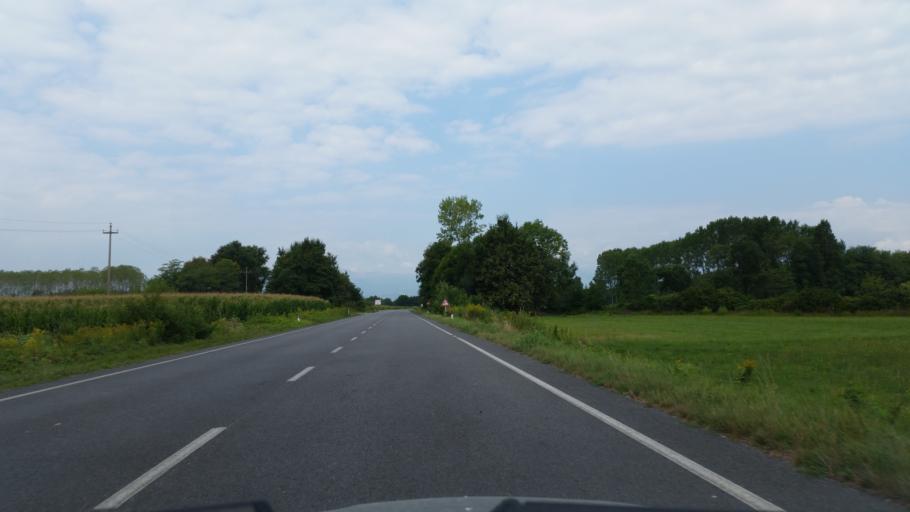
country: IT
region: Piedmont
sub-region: Provincia di Torino
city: Orio Canavese
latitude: 45.3118
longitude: 7.8422
